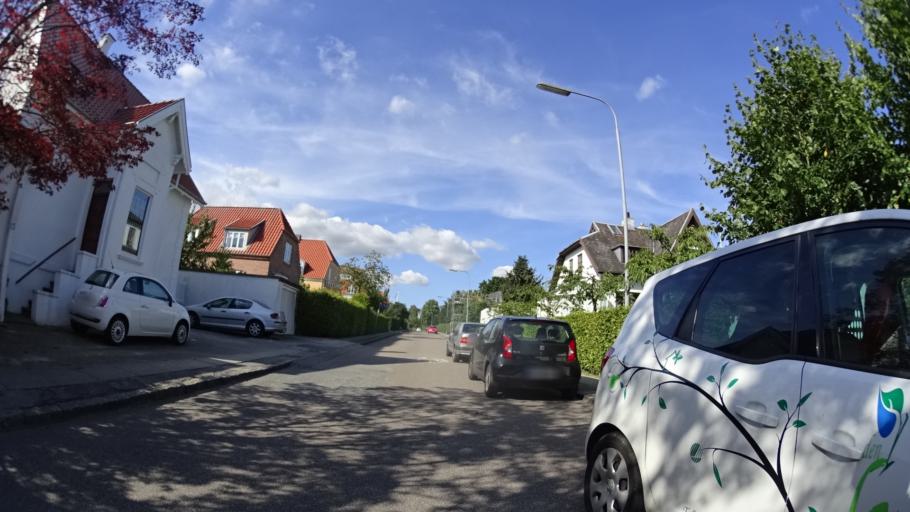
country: DK
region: Central Jutland
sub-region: Arhus Kommune
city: Arhus
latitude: 56.1571
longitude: 10.1699
